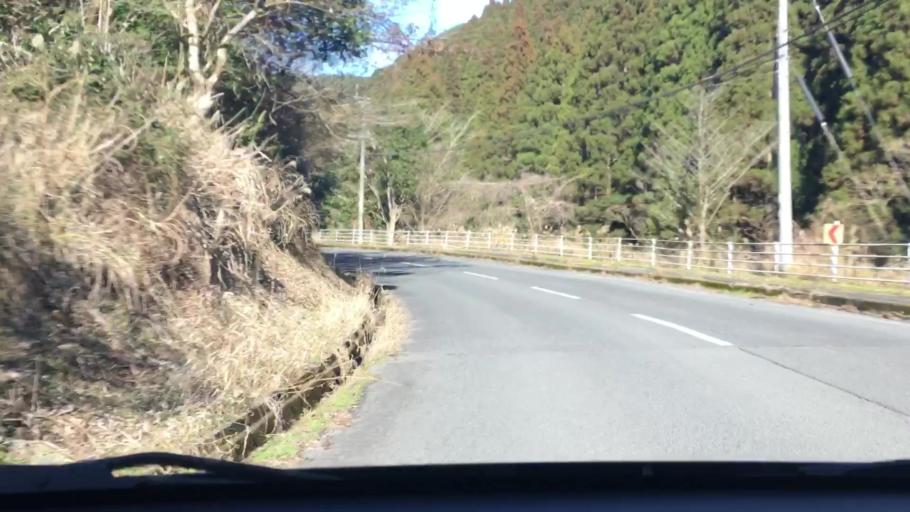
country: JP
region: Kagoshima
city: Satsumasendai
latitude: 31.7499
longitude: 130.4110
